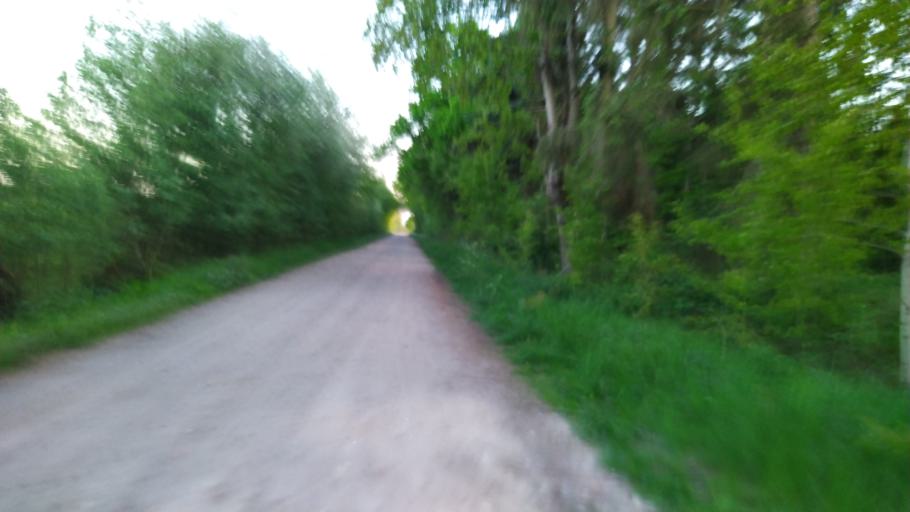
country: DE
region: Lower Saxony
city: Bargstedt
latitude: 53.4875
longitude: 9.4545
